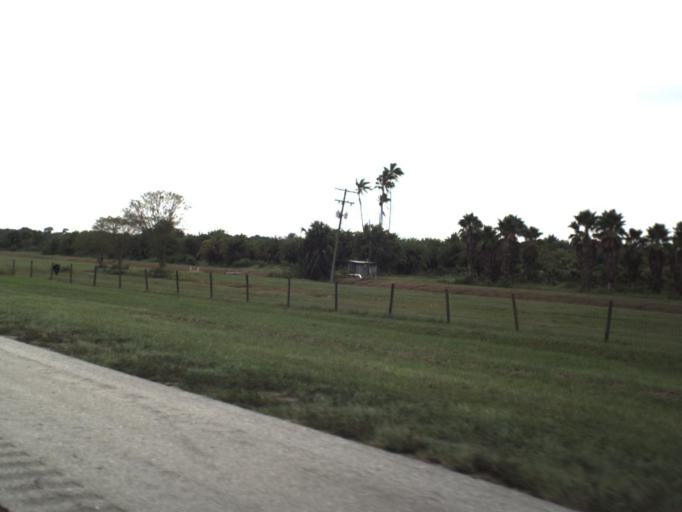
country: US
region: Florida
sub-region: Manatee County
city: Ellenton
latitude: 27.5675
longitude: -82.5148
